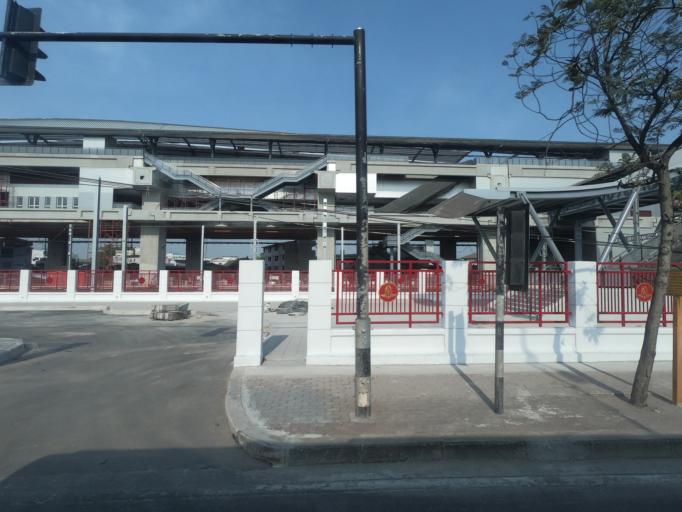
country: TH
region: Bangkok
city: Chatuchak
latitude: 13.8267
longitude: 100.5502
